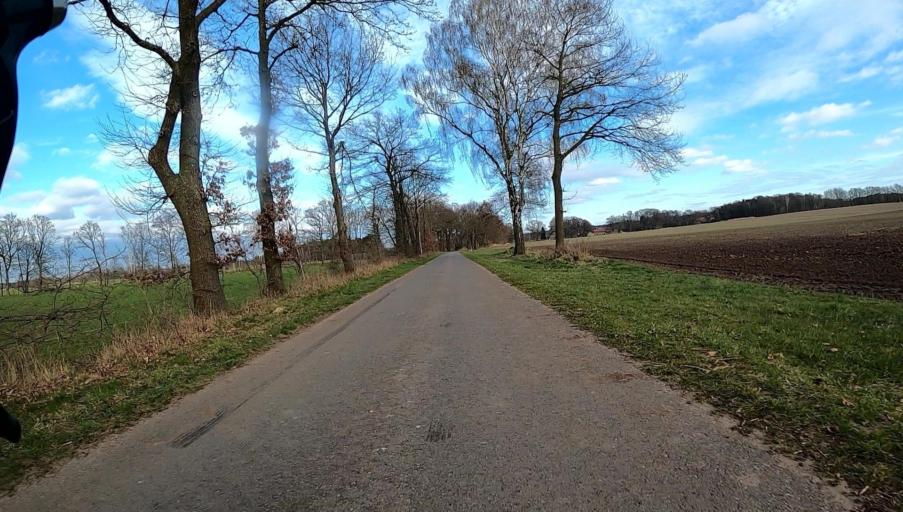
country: DE
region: Lower Saxony
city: Lindwedel
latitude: 52.5862
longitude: 9.6322
